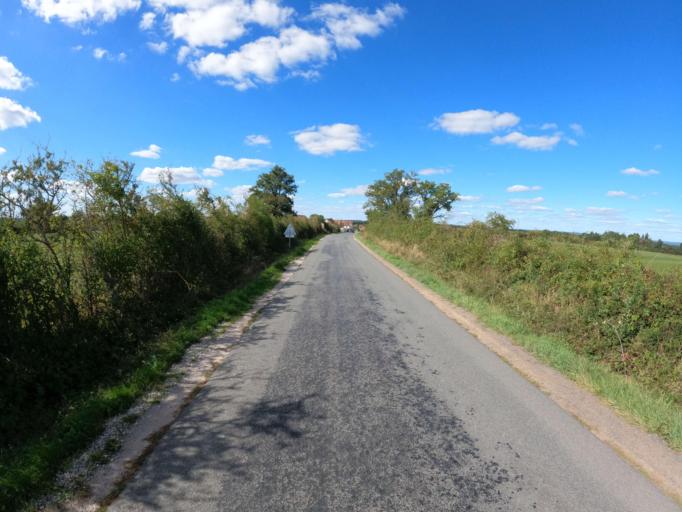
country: FR
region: Auvergne
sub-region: Departement de l'Allier
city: Doyet
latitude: 46.4055
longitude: 2.7403
